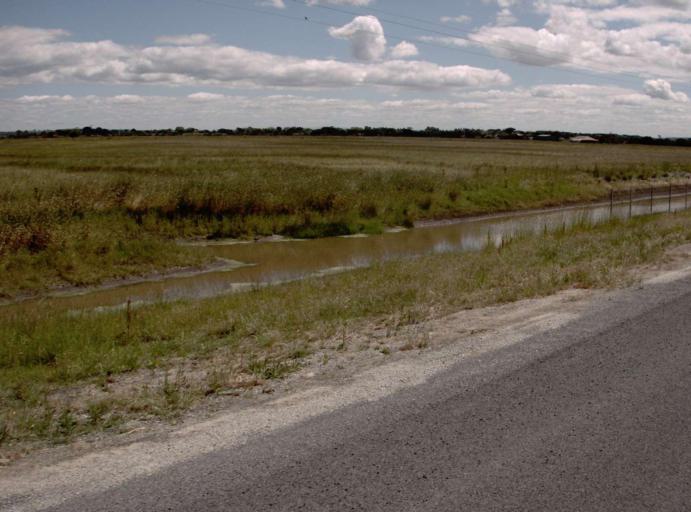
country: AU
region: Victoria
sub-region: Bass Coast
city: North Wonthaggi
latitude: -38.5045
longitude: 145.4552
